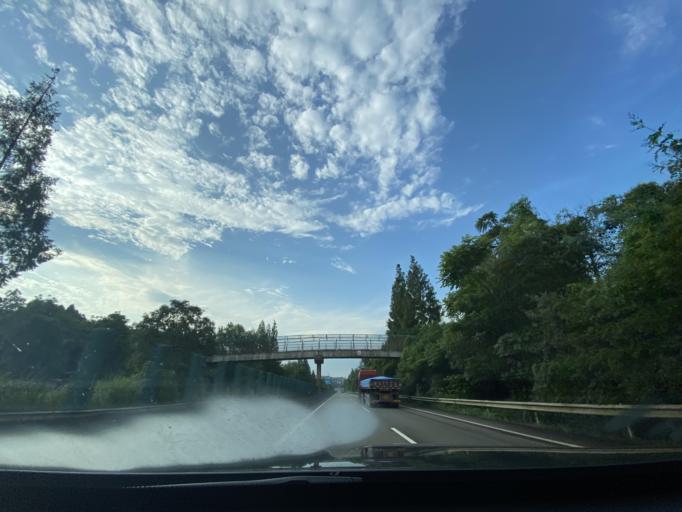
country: CN
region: Sichuan
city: Jiancheng
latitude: 30.3324
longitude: 104.5661
